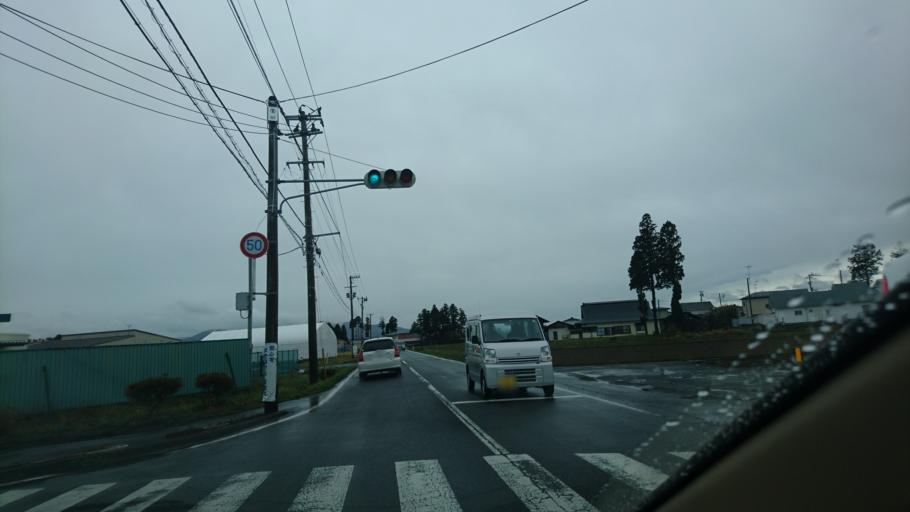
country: JP
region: Iwate
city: Mizusawa
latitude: 39.1078
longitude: 141.1562
